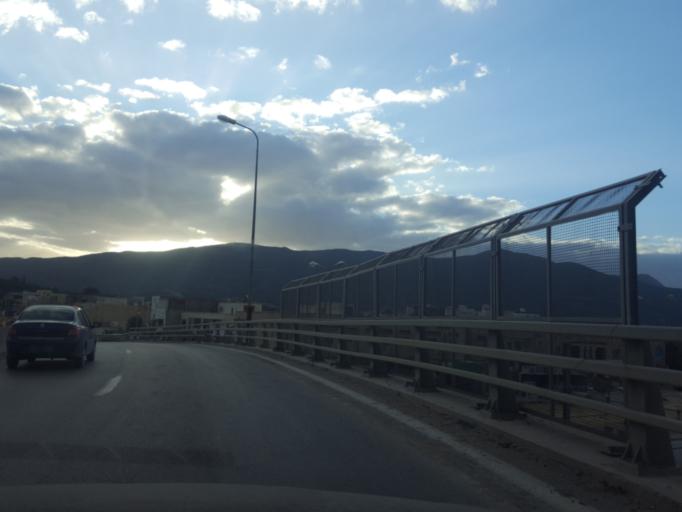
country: TN
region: Tunis
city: Hammam-Lif
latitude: 36.7011
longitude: 10.4034
